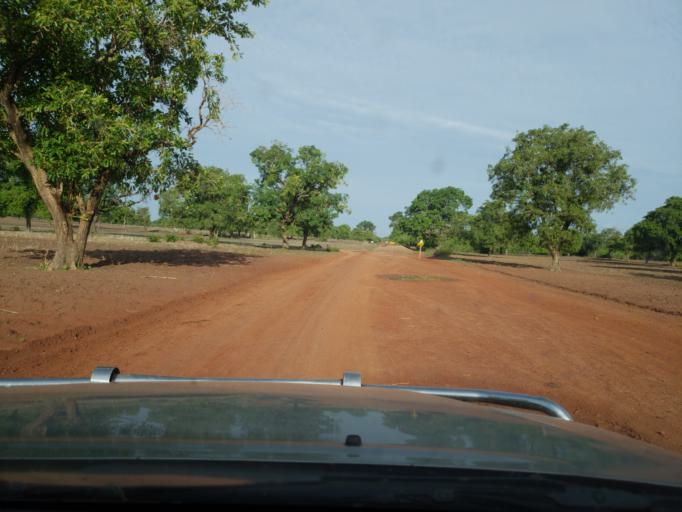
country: ML
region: Sikasso
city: Koutiala
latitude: 12.4191
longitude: -5.7025
